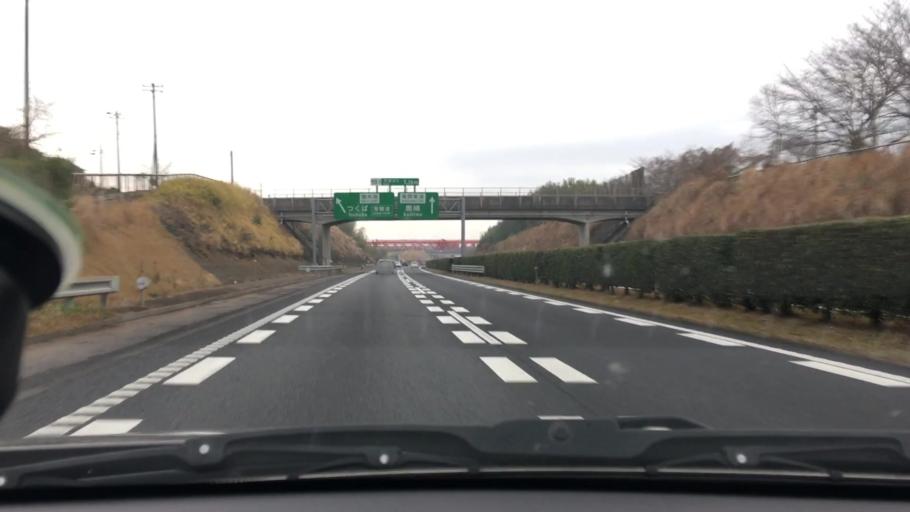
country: JP
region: Chiba
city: Narita
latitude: 35.8067
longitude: 140.3720
